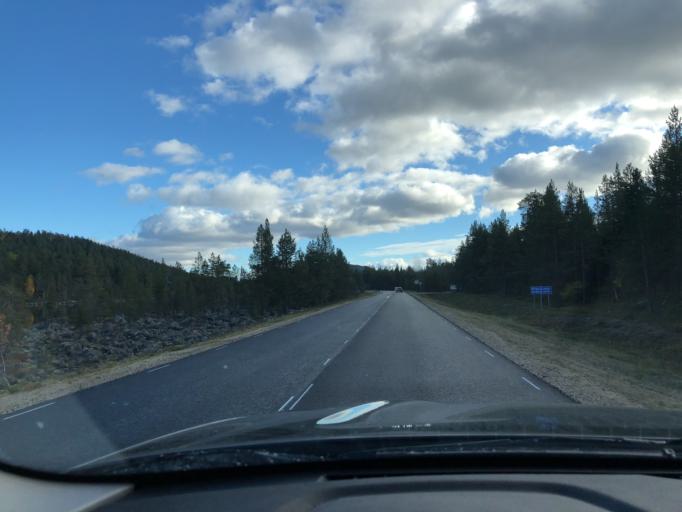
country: FI
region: Lapland
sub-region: Pohjois-Lappi
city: Inari
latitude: 68.8256
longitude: 27.2910
